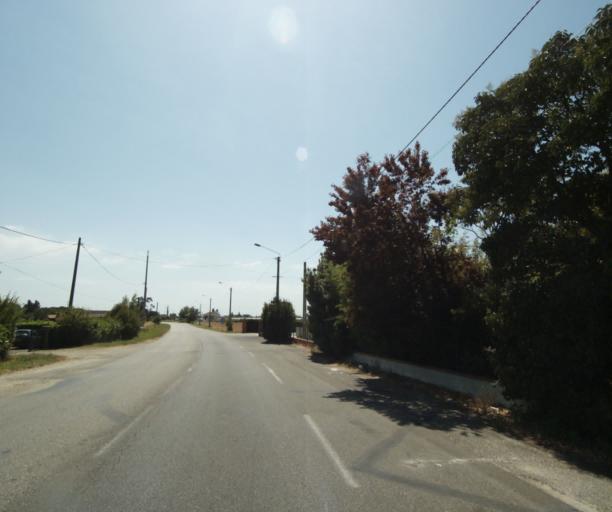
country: FR
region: Midi-Pyrenees
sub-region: Departement du Tarn-et-Garonne
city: Montauban
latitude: 43.9985
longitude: 1.3524
